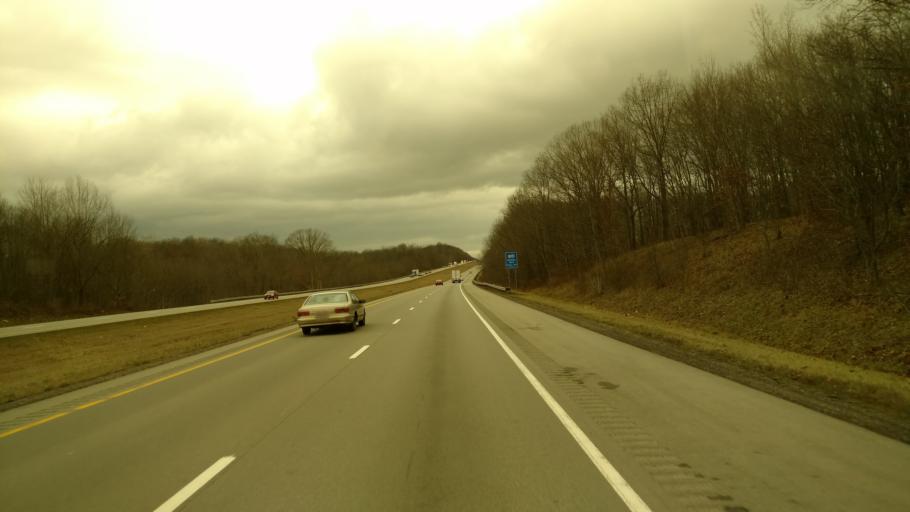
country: US
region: Ohio
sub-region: Muskingum County
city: Zanesville
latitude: 39.9474
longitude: -82.1486
